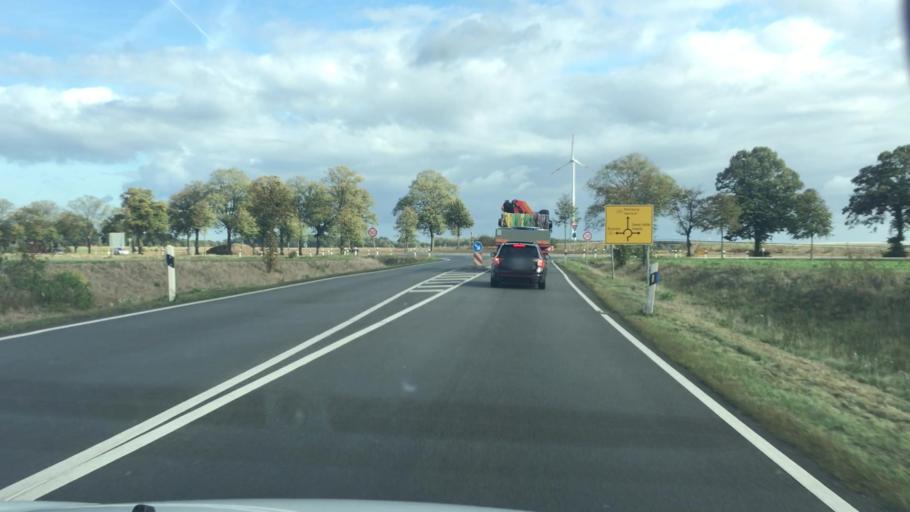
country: DE
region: Lower Saxony
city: Diepholz
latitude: 52.6277
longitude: 8.3986
